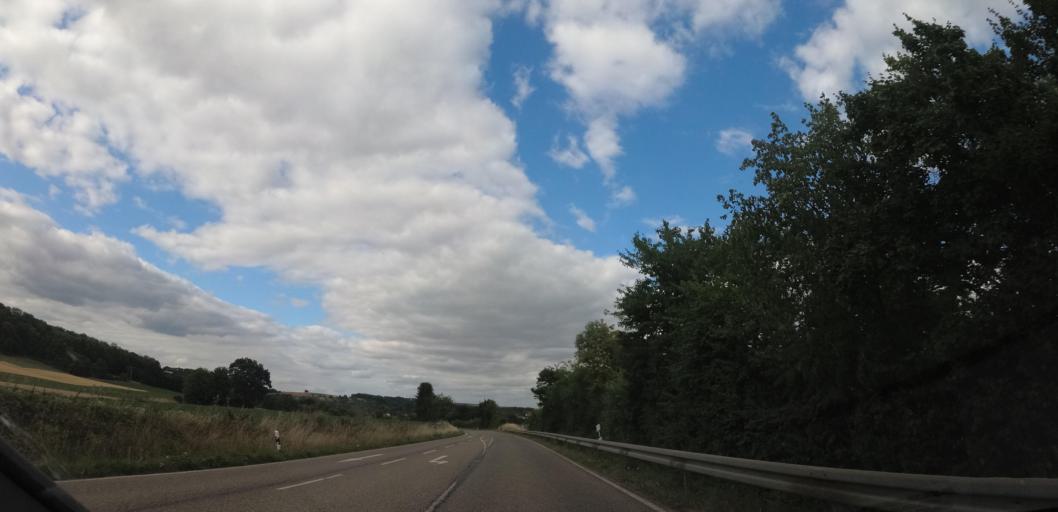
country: DE
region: Baden-Wuerttemberg
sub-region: Regierungsbezirk Stuttgart
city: Neudenau
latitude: 49.2912
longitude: 9.2929
